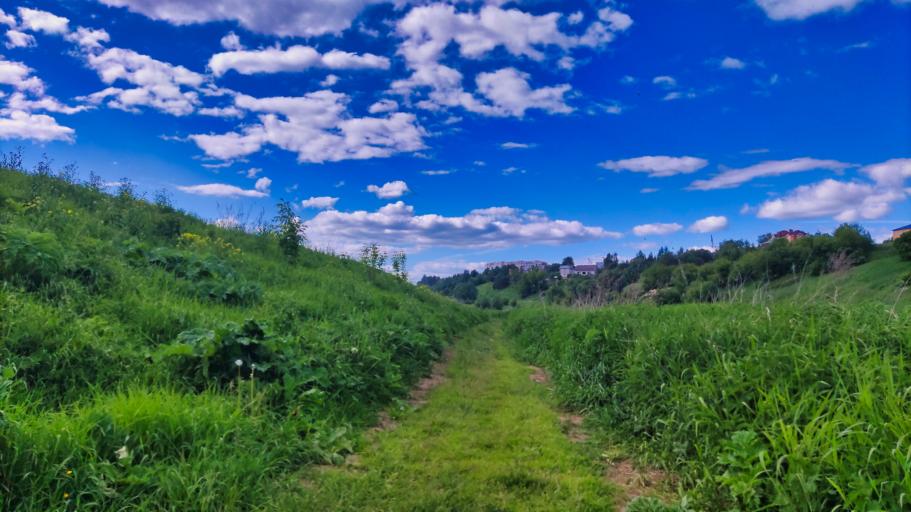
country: RU
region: Tverskaya
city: Rzhev
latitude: 56.2490
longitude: 34.3492
